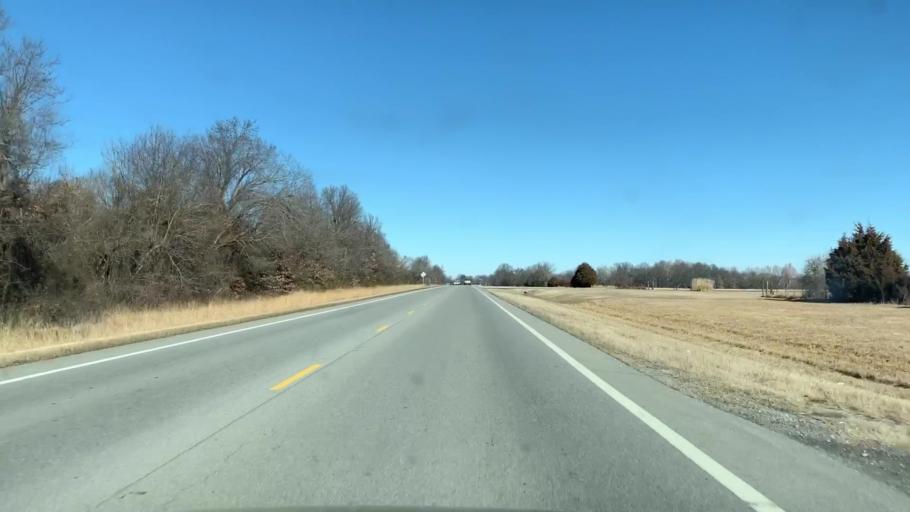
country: US
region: Kansas
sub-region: Cherokee County
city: Baxter Springs
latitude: 37.0433
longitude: -94.7355
